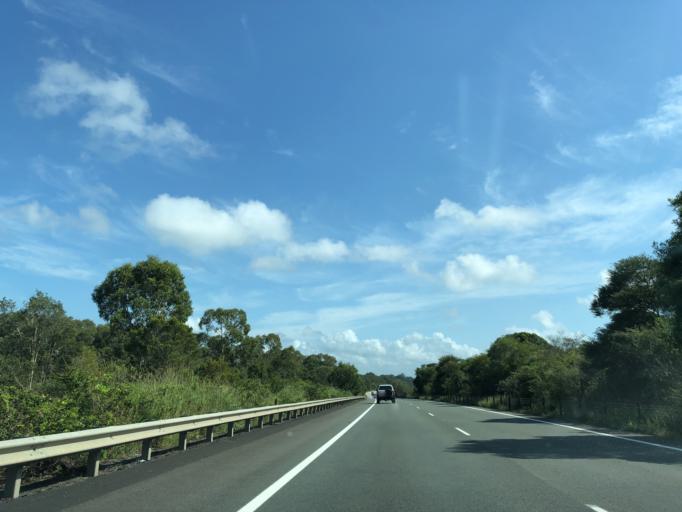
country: AU
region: New South Wales
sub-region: Byron Shire
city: Brunswick Heads
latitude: -28.6035
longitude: 153.5457
